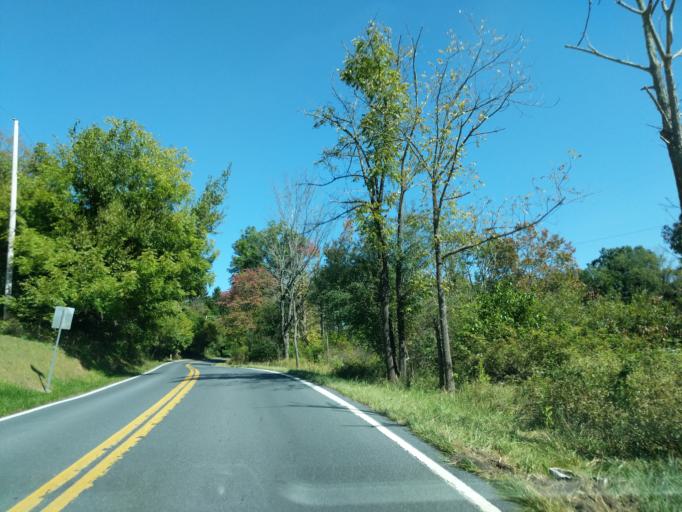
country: US
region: Pennsylvania
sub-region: Bucks County
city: Spinnerstown
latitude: 40.4605
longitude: -75.4816
